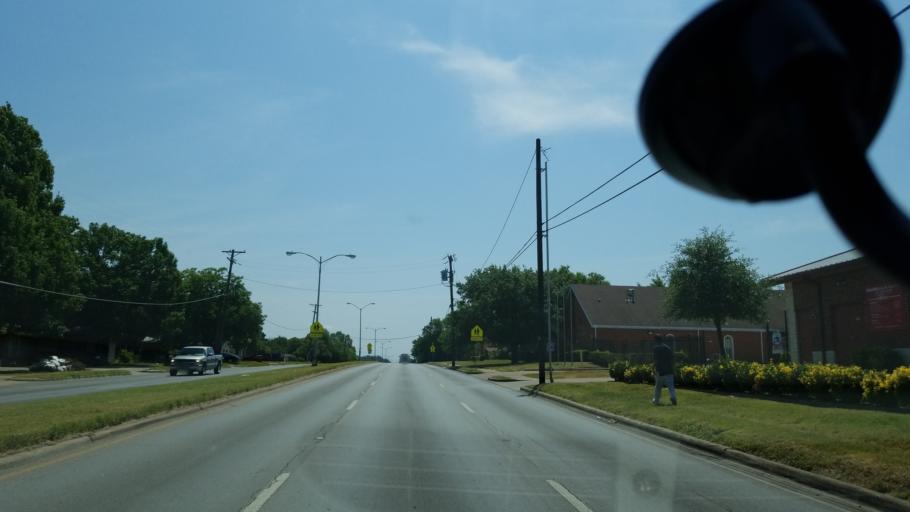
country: US
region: Texas
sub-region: Dallas County
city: Cockrell Hill
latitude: 32.7203
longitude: -96.8641
